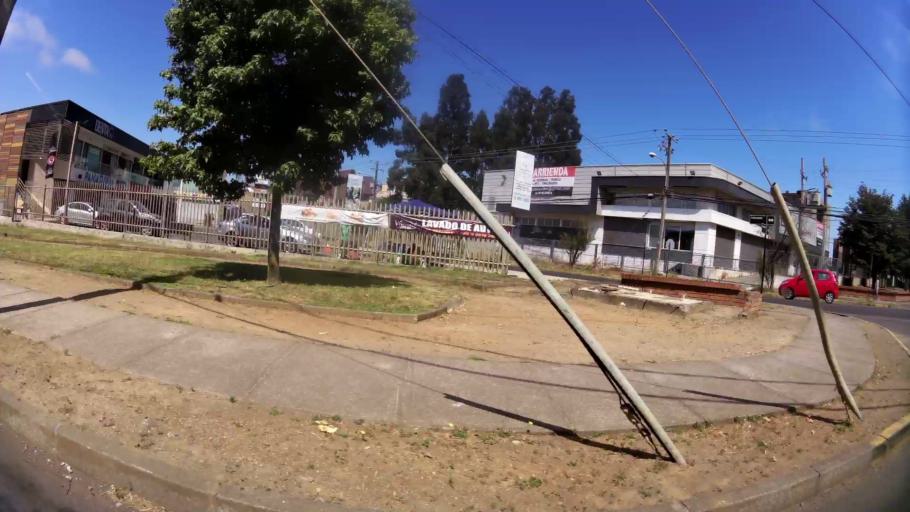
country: CL
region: Biobio
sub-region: Provincia de Concepcion
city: Concepcion
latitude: -36.7803
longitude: -73.0445
